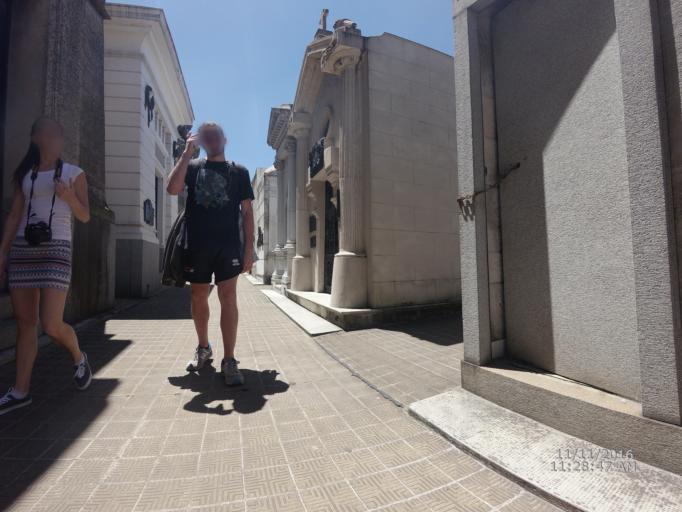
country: AR
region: Buenos Aires F.D.
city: Retiro
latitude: -34.5875
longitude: -58.3948
